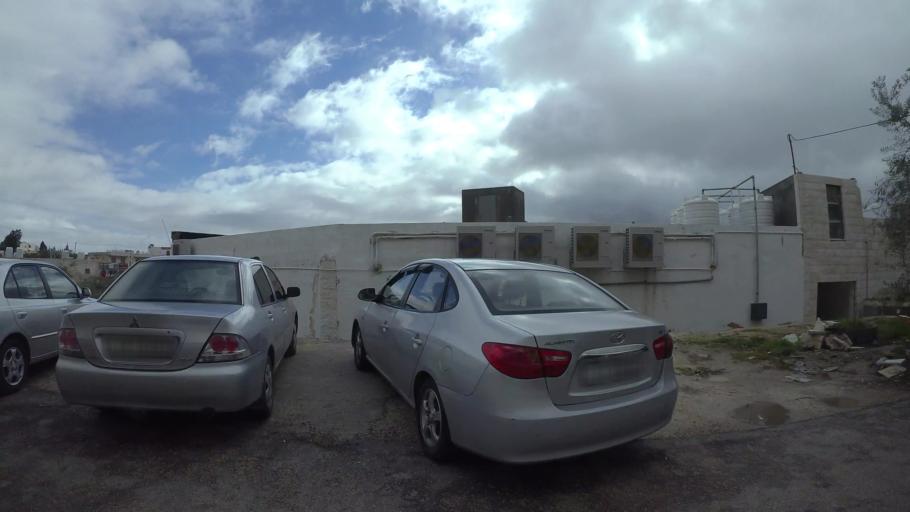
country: JO
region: Amman
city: Al Jubayhah
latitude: 32.0581
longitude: 35.8918
